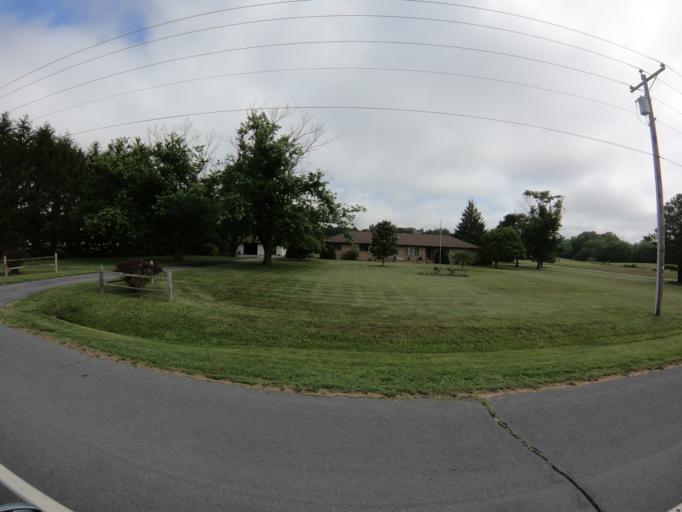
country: US
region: Delaware
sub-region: Kent County
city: Riverview
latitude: 39.0055
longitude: -75.5408
